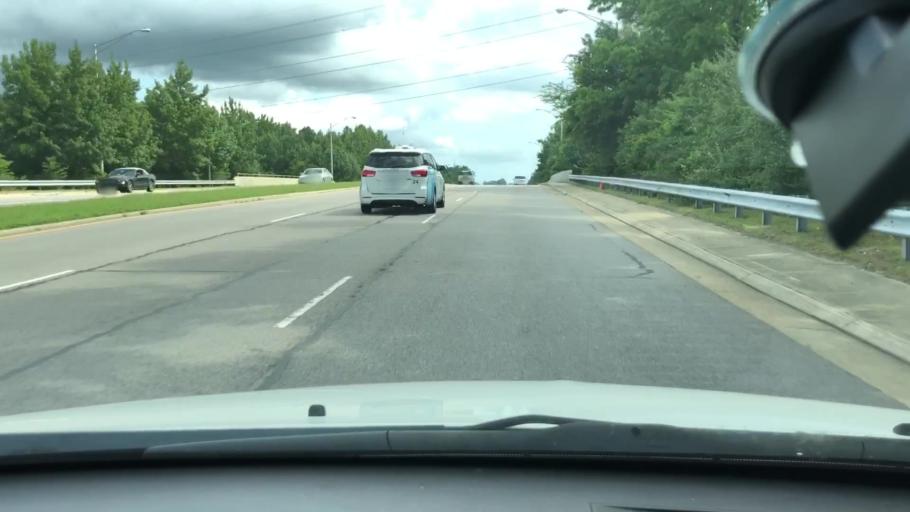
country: US
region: Virginia
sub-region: City of Chesapeake
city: Chesapeake
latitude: 36.7865
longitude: -76.2524
